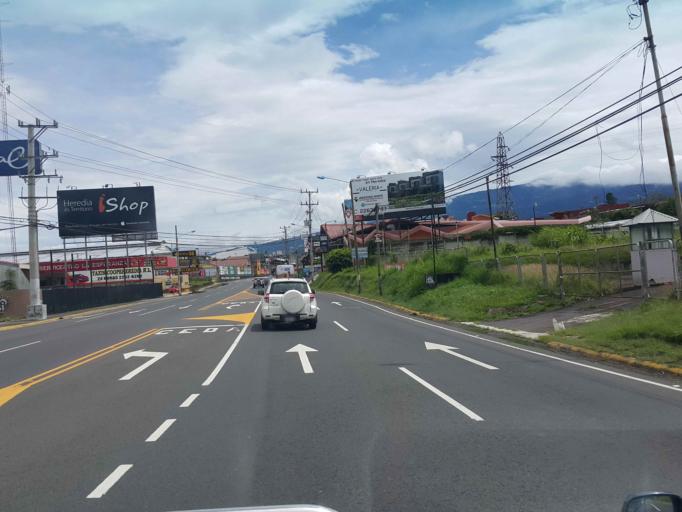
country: CR
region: Heredia
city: Heredia
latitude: 9.9881
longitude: -84.1107
